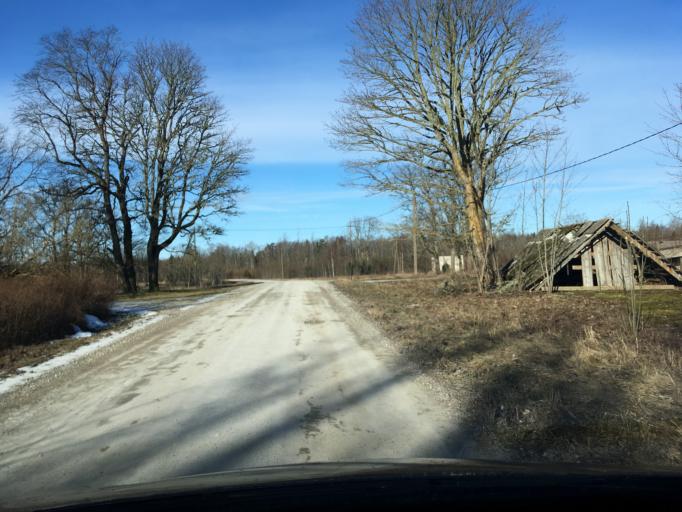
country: EE
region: Laeaene
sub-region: Lihula vald
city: Lihula
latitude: 58.5680
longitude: 23.6630
